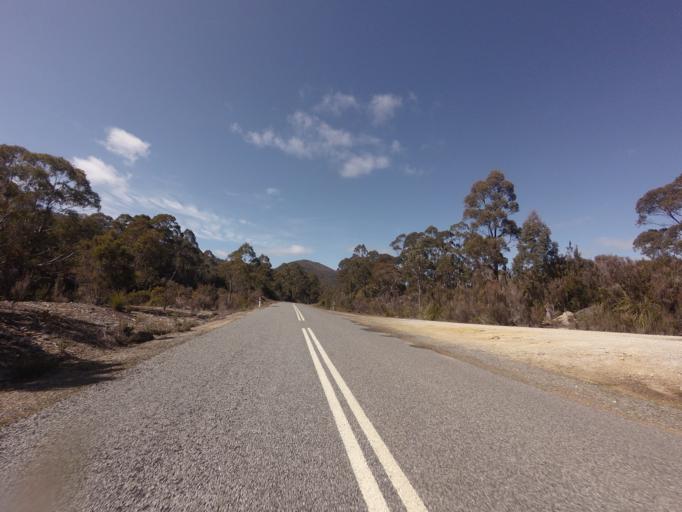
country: AU
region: Tasmania
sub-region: Huon Valley
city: Geeveston
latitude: -42.7721
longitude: 146.3972
